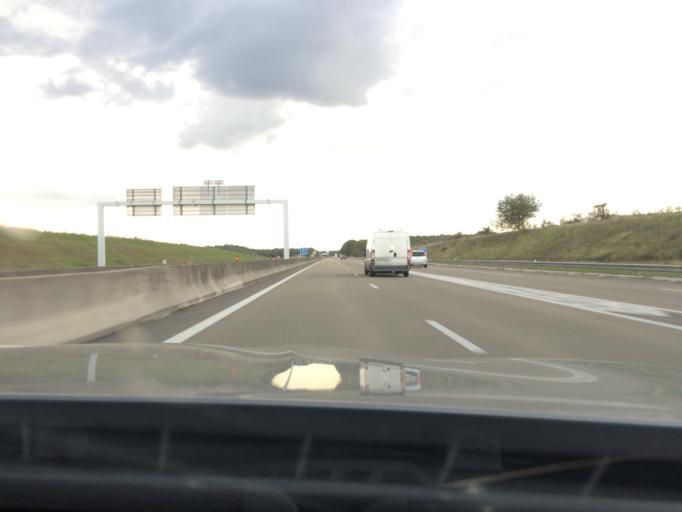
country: FR
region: Ile-de-France
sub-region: Departement de Seine-et-Marne
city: Souppes-sur-Loing
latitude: 48.2267
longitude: 2.7624
